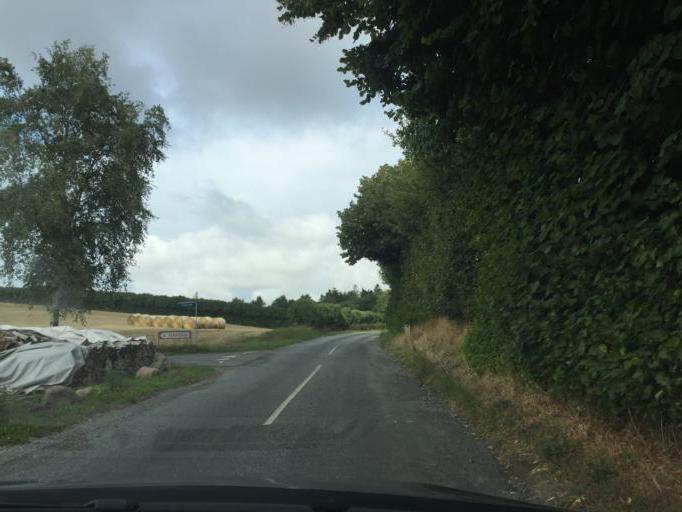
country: DK
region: South Denmark
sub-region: Assens Kommune
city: Harby
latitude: 55.1944
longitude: 10.1991
